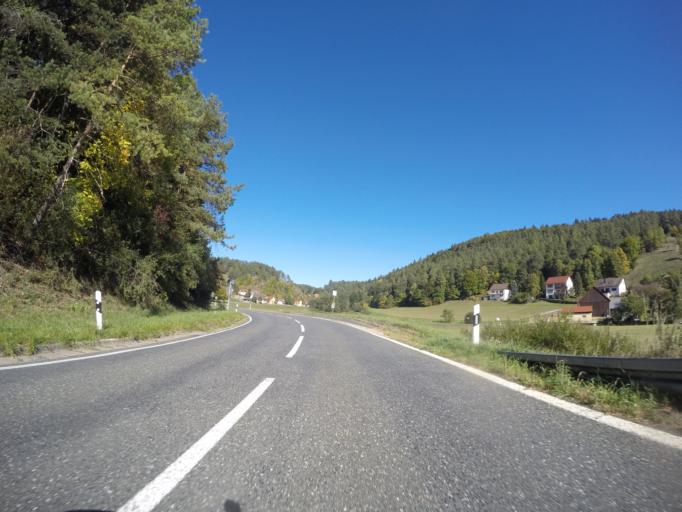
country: DE
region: Bavaria
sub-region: Upper Franconia
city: Waischenfeld
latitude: 49.8078
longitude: 11.3441
